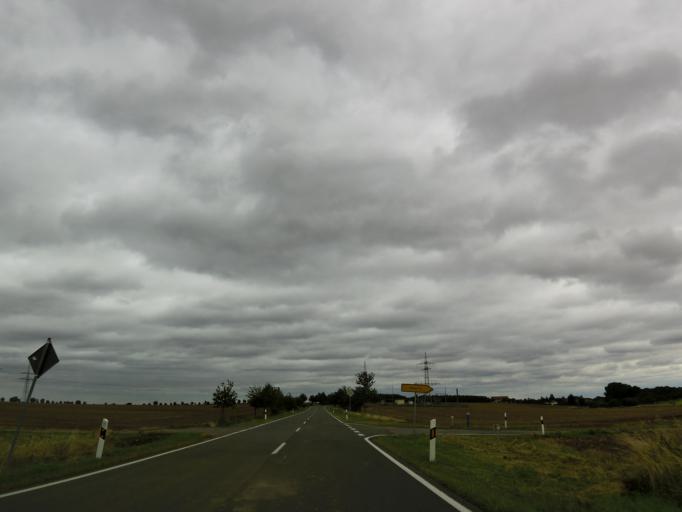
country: DE
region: Saxony-Anhalt
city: Teuchern
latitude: 51.1005
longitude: 11.9865
